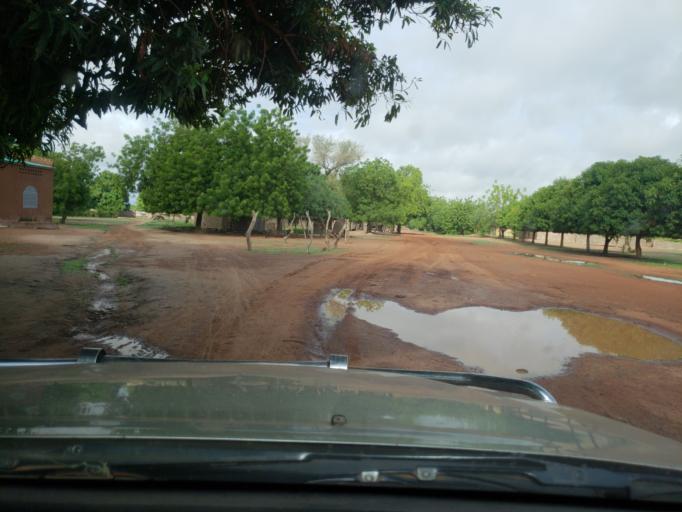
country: ML
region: Sikasso
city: Koutiala
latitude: 12.3914
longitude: -6.0257
